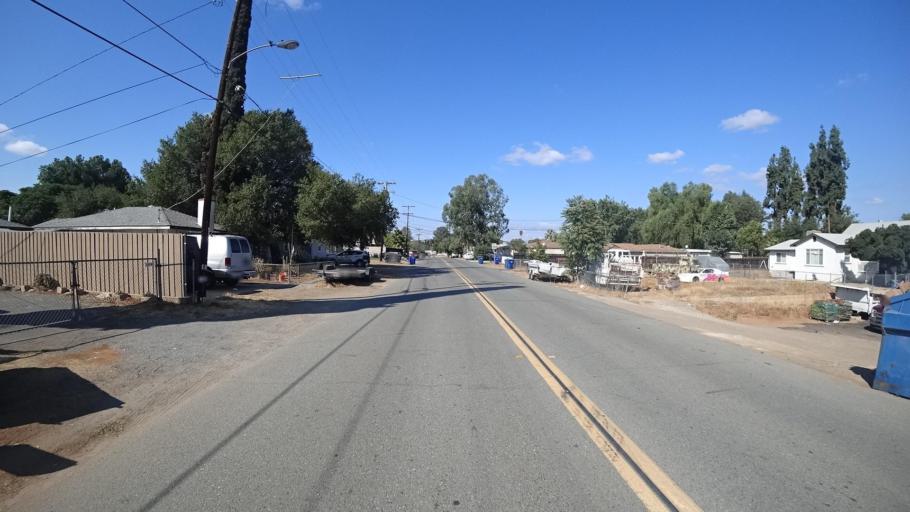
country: US
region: California
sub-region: San Diego County
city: Lakeside
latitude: 32.8568
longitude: -116.9164
